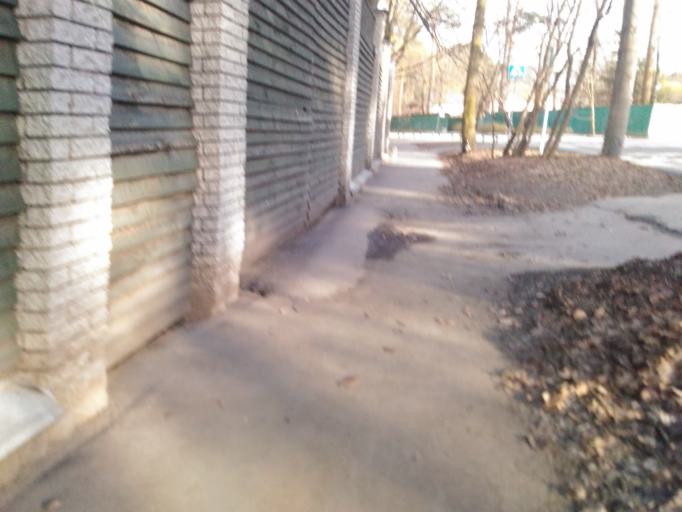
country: RU
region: Moscow
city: Strogino
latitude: 55.7864
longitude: 37.4199
